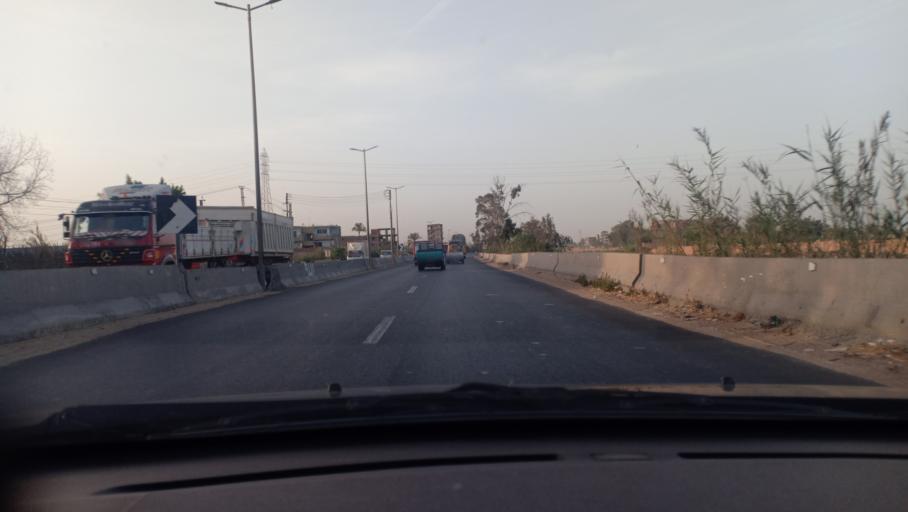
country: EG
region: Muhafazat al Minufiyah
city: Quwaysina
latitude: 30.5574
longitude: 31.2682
